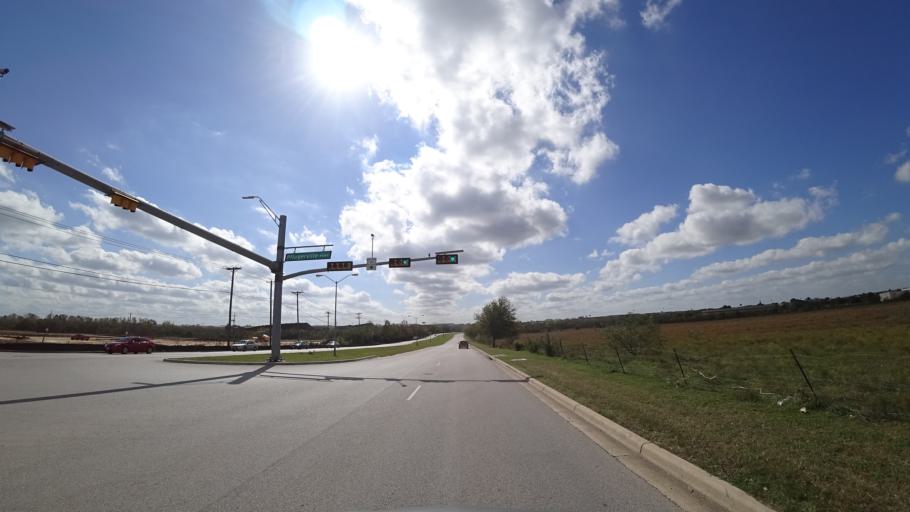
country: US
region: Texas
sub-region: Travis County
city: Windemere
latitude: 30.4776
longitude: -97.6641
